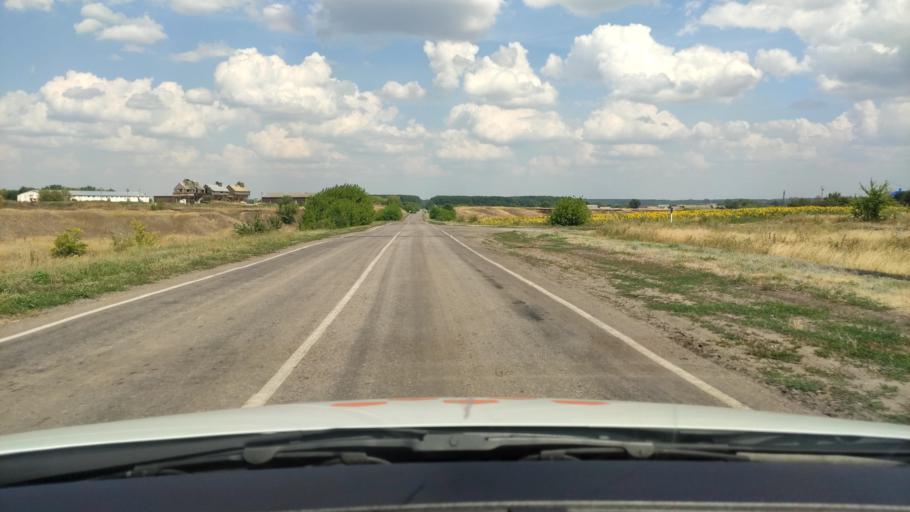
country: RU
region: Voronezj
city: Sadovoye
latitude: 51.7664
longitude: 40.4779
